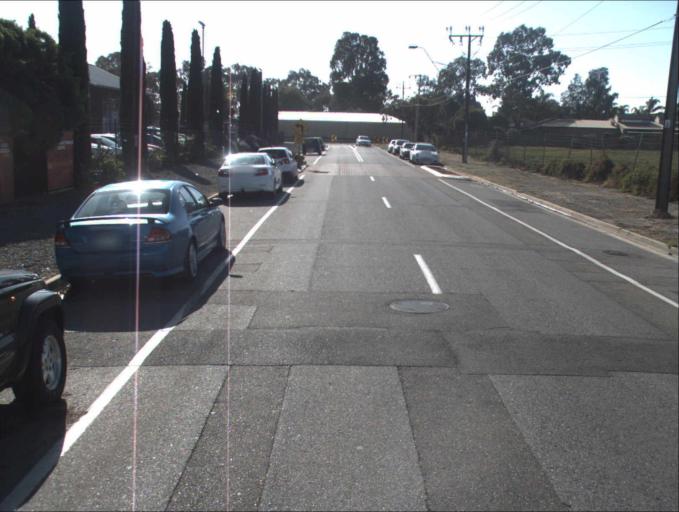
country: AU
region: South Australia
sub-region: Port Adelaide Enfield
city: Alberton
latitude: -34.8431
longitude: 138.5387
